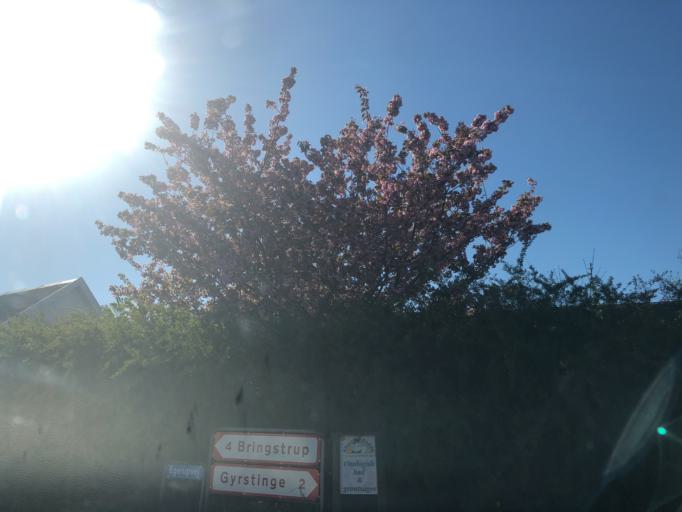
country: DK
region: Zealand
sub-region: Ringsted Kommune
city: Ringsted
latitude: 55.4676
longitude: 11.6868
